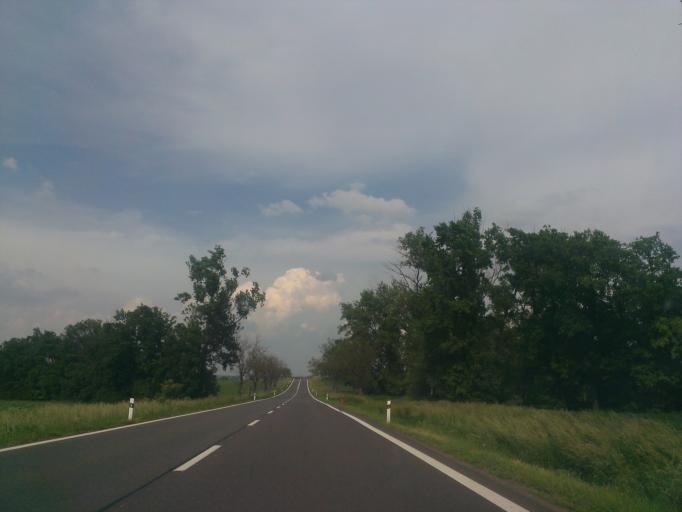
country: CZ
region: South Moravian
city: Miroslav
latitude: 48.9132
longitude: 16.3237
